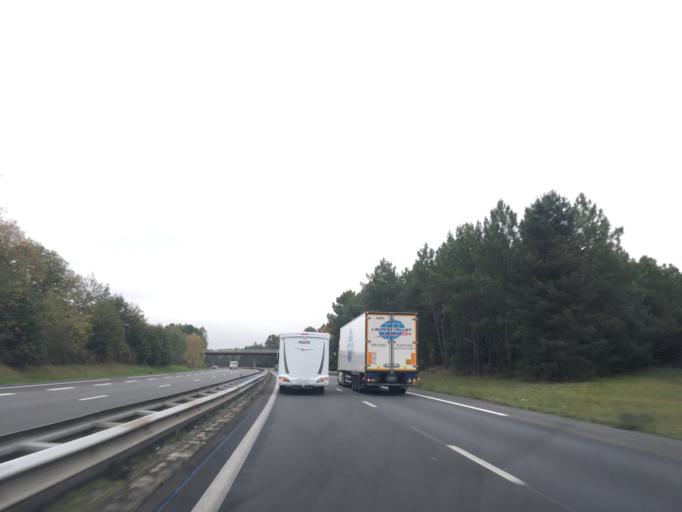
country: FR
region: Pays de la Loire
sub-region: Departement de Maine-et-Loire
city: Seiches-sur-le-Loir
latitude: 47.5623
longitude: -0.3305
